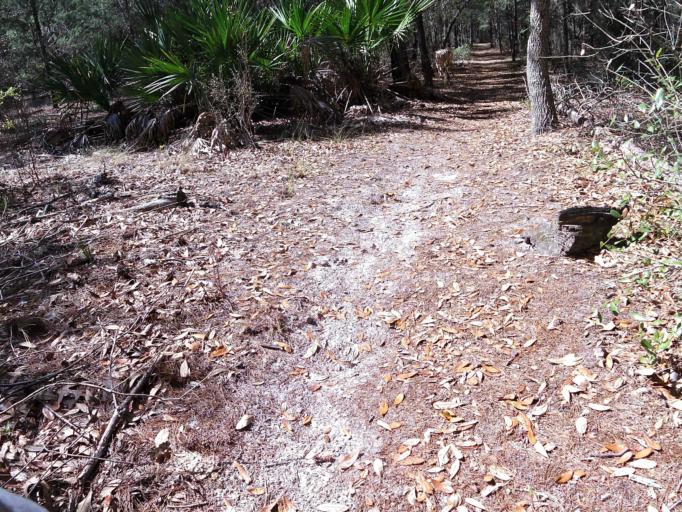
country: US
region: Florida
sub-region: Putnam County
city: Interlachen
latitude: 29.7629
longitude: -81.8550
